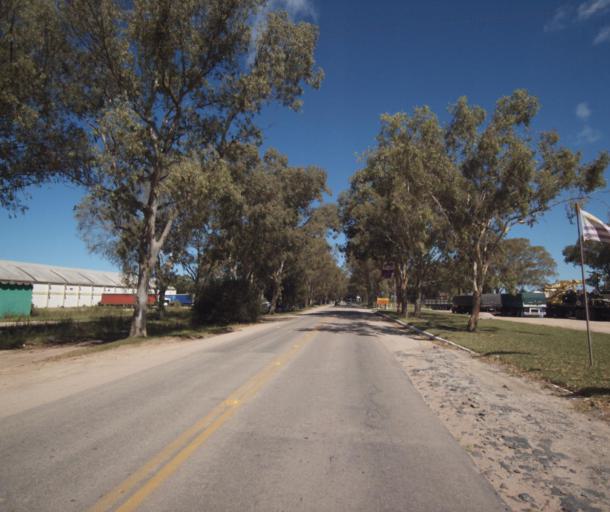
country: BR
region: Rio Grande do Sul
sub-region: Chui
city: Chui
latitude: -33.6860
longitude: -53.4483
